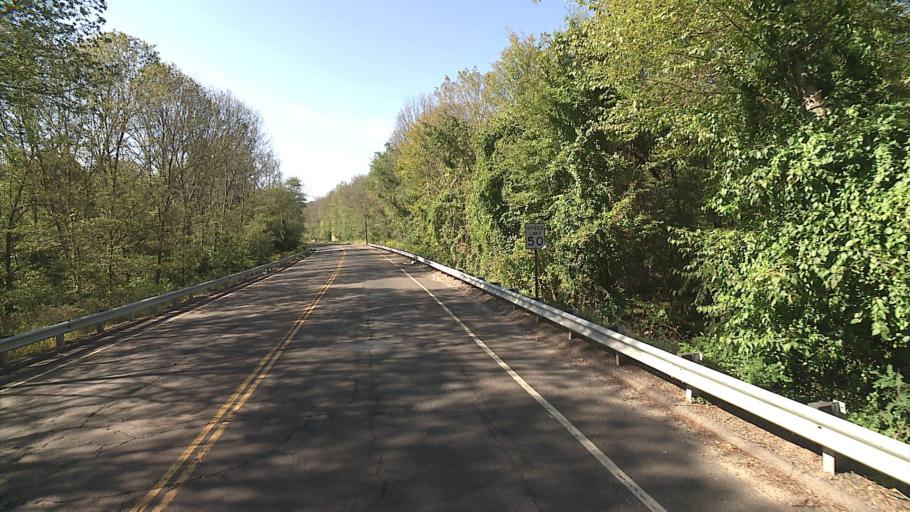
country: US
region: Connecticut
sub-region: Middlesex County
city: Higganum
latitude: 41.5298
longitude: -72.5652
